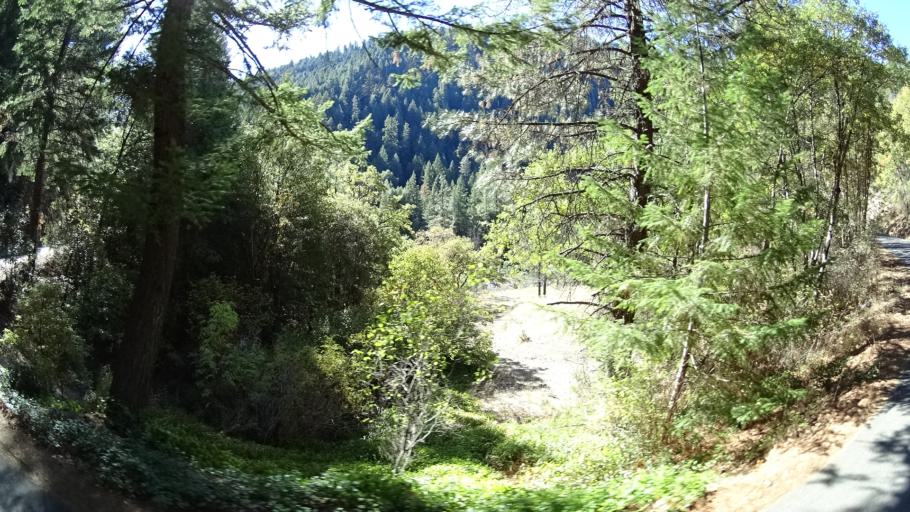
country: US
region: California
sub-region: Trinity County
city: Weaverville
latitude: 41.1436
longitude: -123.1837
